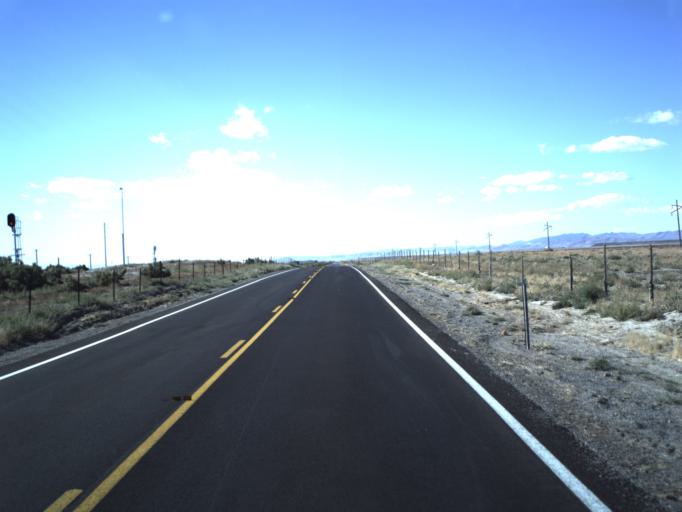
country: US
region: Utah
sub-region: Millard County
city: Delta
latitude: 39.2281
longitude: -112.6706
